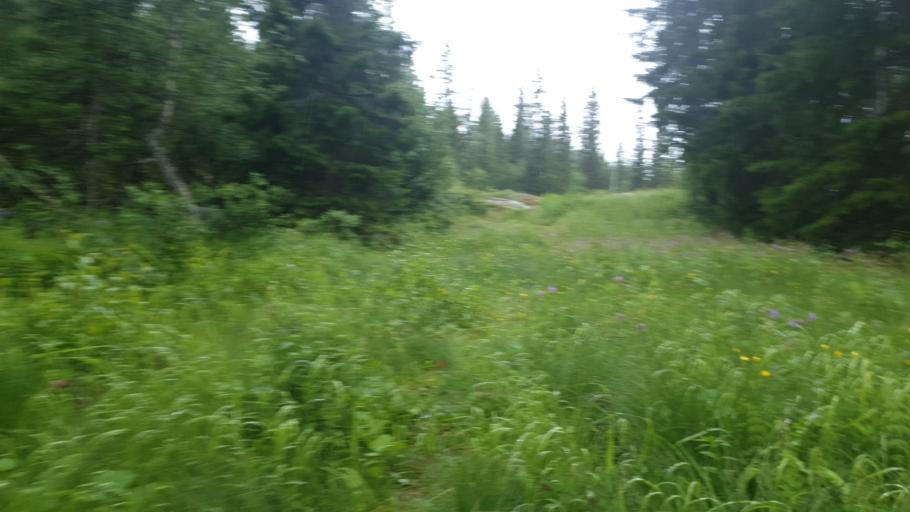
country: NO
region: Oppland
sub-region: Vestre Slidre
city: Slidre
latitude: 61.2308
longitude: 8.9136
